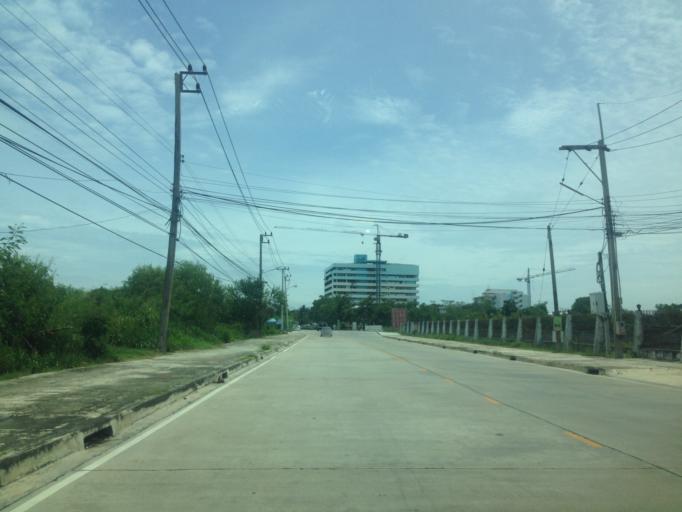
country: TH
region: Chon Buri
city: Chon Buri
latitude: 13.3449
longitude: 100.9567
